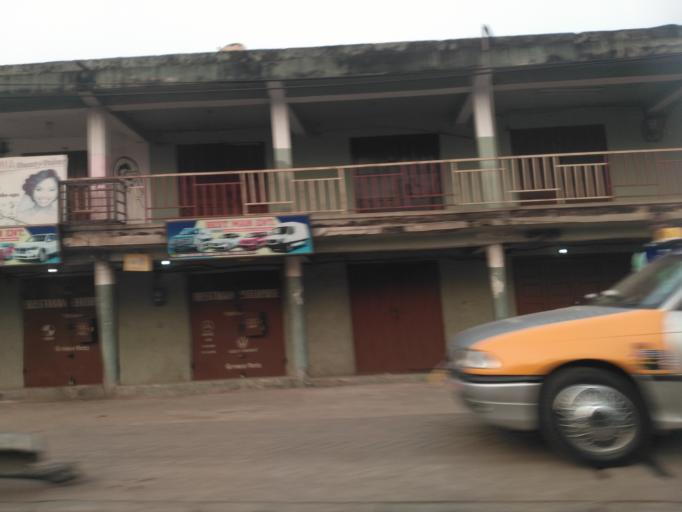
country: GH
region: Ashanti
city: Kumasi
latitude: 6.6836
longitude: -1.6110
